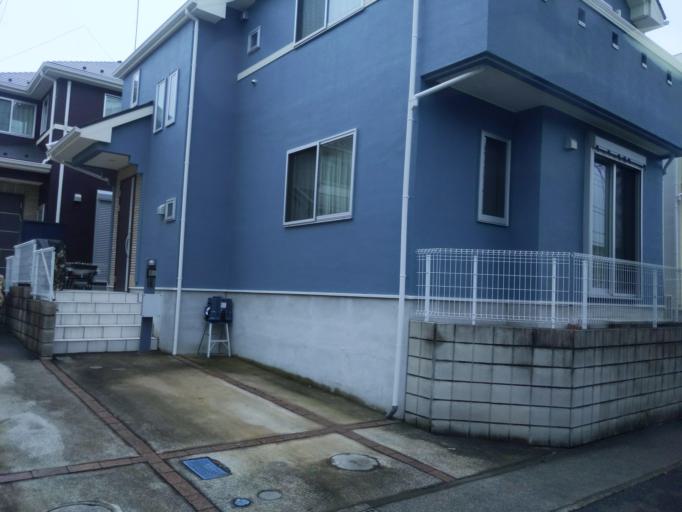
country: JP
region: Tokyo
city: Chofugaoka
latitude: 35.6018
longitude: 139.5691
